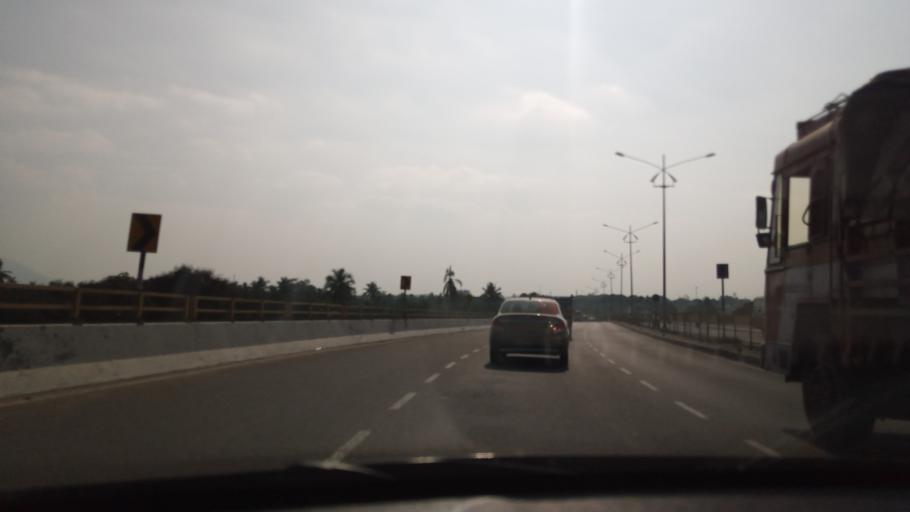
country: IN
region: Tamil Nadu
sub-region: Vellore
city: Vaniyambadi
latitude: 12.6830
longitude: 78.6292
